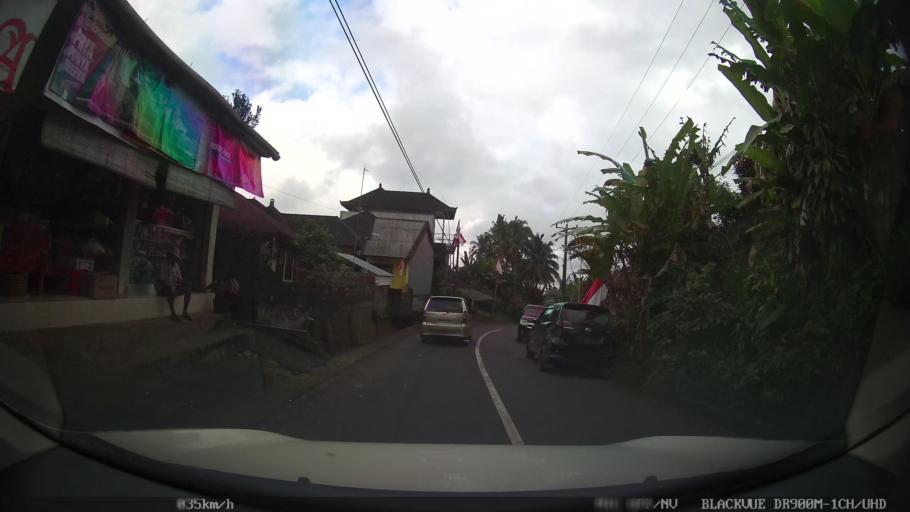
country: ID
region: Bali
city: Peneng
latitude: -8.3543
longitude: 115.1847
